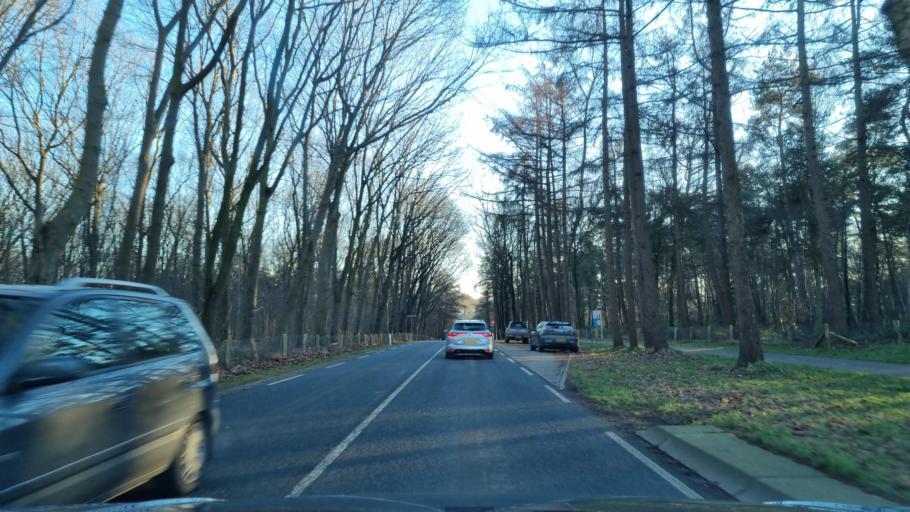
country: NL
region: Gelderland
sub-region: Gemeente Groesbeek
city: Berg en Dal
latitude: 51.8033
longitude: 5.9276
